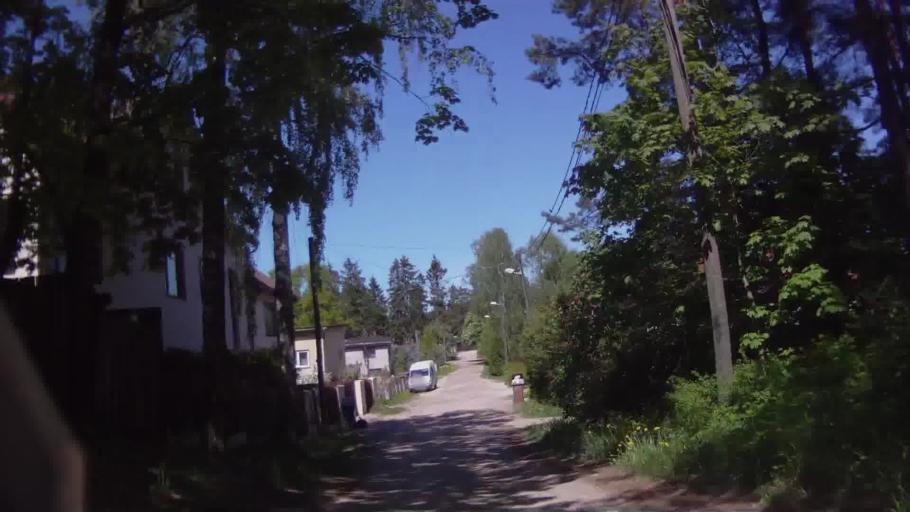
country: LV
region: Riga
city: Bergi
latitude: 56.9871
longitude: 24.2988
